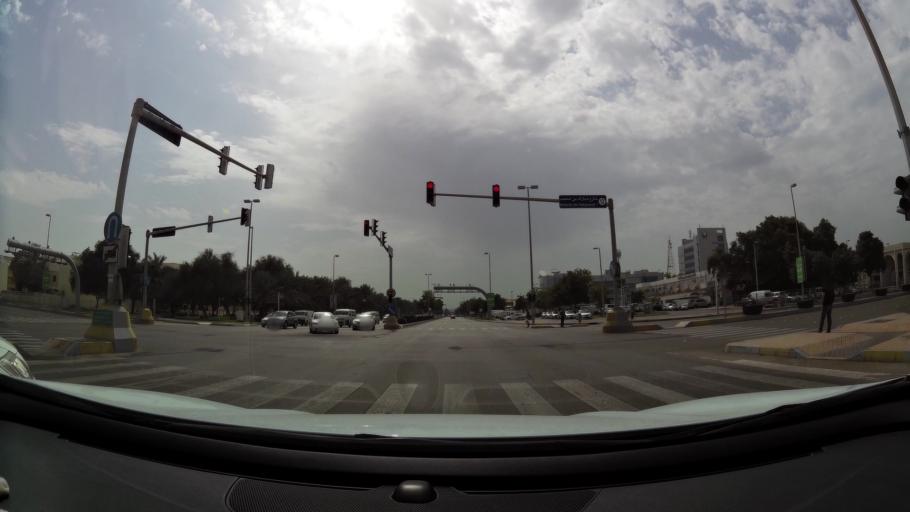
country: AE
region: Abu Dhabi
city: Abu Dhabi
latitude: 24.4620
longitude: 54.3614
